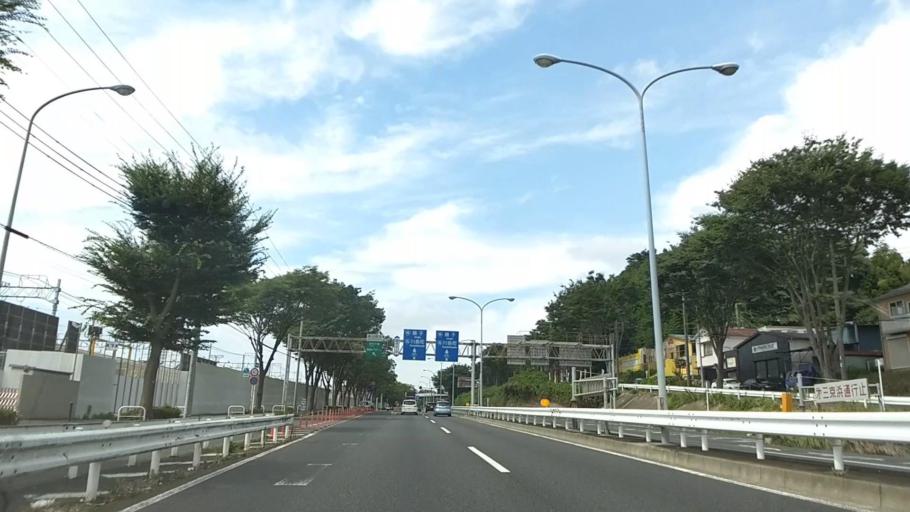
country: JP
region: Kanagawa
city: Yokohama
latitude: 35.4845
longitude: 139.5893
